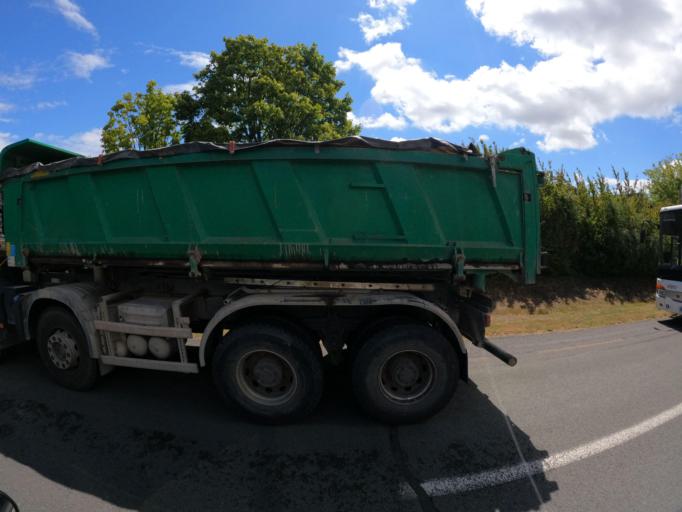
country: FR
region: Pays de la Loire
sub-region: Departement de Maine-et-Loire
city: Avrille
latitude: 47.5196
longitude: -0.6121
